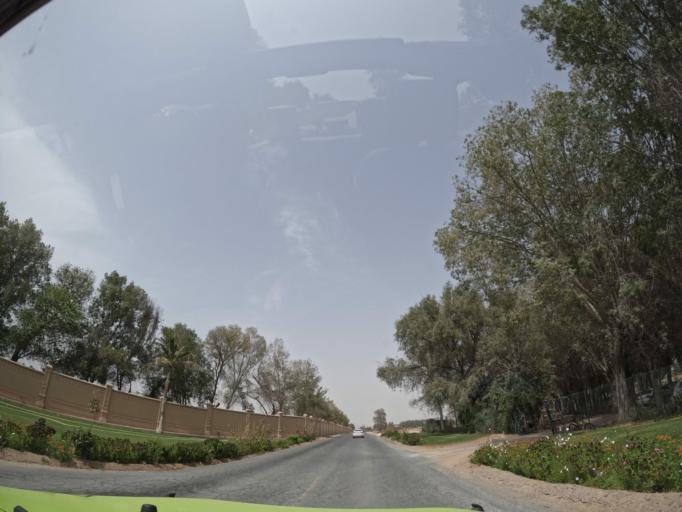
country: AE
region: Dubai
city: Dubai
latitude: 25.1357
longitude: 55.3370
